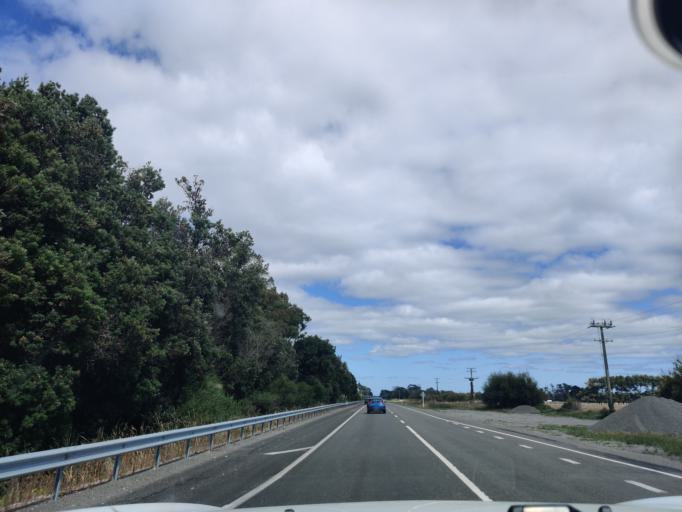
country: NZ
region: Manawatu-Wanganui
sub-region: Palmerston North City
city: Palmerston North
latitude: -40.3923
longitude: 175.5236
